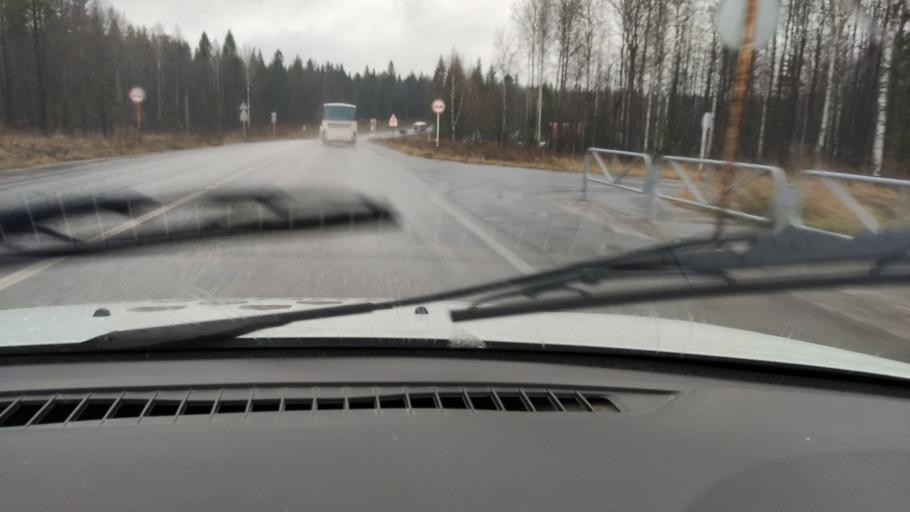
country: RU
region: Perm
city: Novyye Lyady
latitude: 58.0468
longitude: 56.5467
